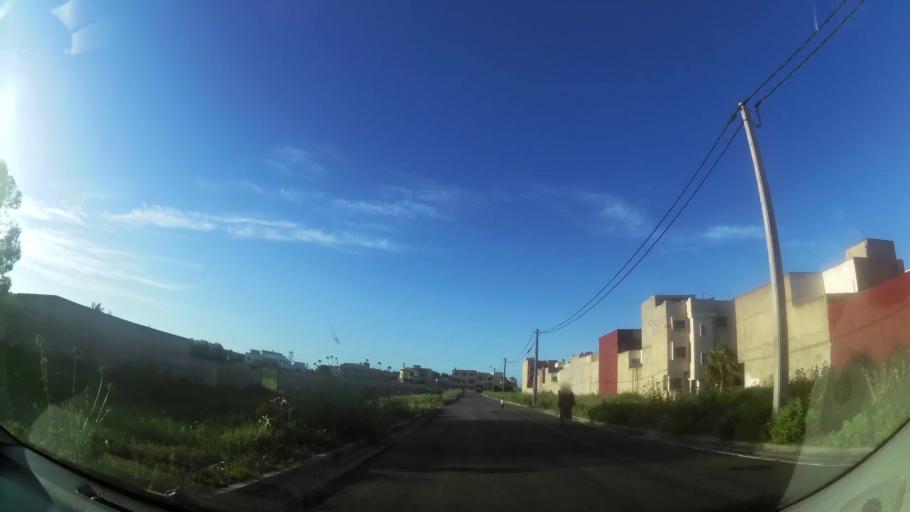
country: MA
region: Oriental
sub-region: Berkane-Taourirt
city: Madagh
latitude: 35.0830
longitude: -2.2402
